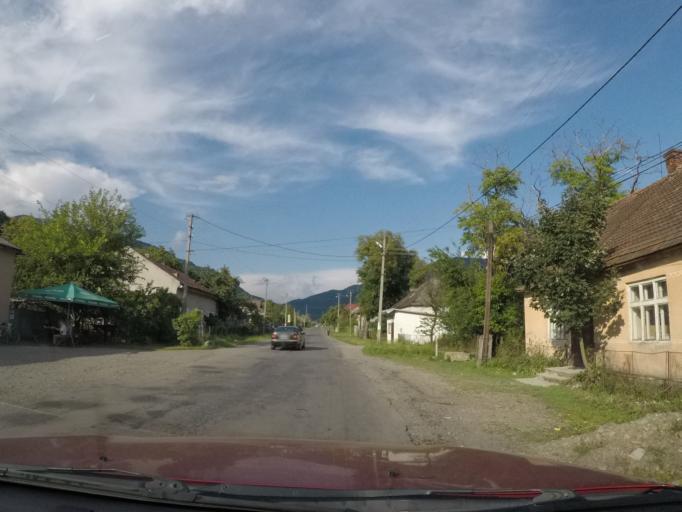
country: UA
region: Zakarpattia
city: Velykyi Bereznyi
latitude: 48.9437
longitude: 22.5968
